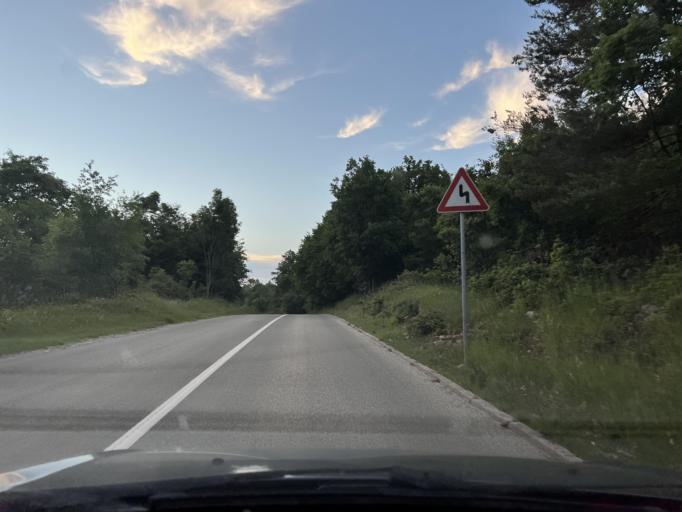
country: HR
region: Primorsko-Goranska
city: Klana
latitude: 45.4552
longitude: 14.3147
